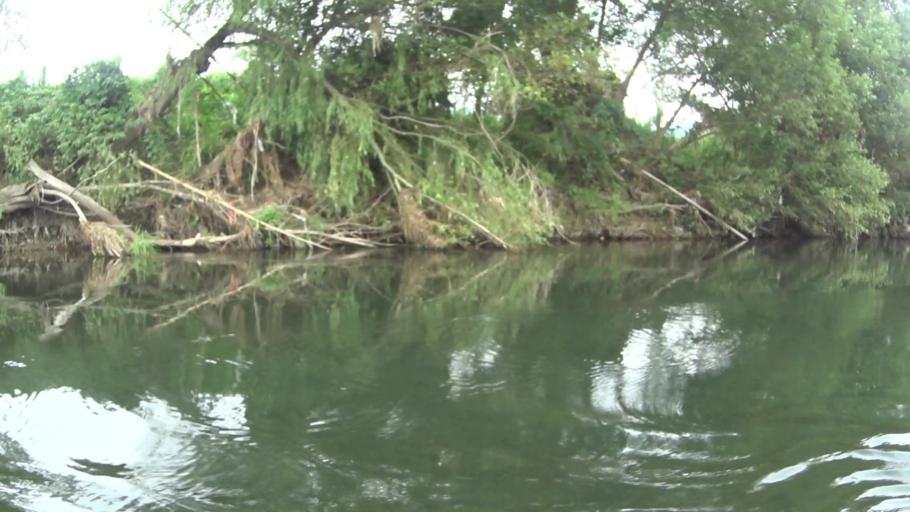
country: JP
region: Kyoto
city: Kameoka
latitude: 35.0173
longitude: 135.5927
